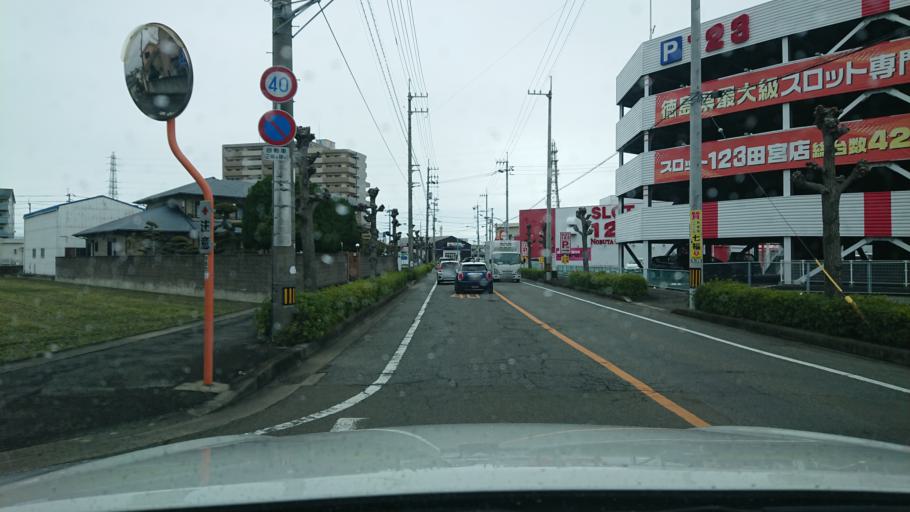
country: JP
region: Tokushima
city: Tokushima-shi
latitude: 34.0853
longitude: 134.5386
